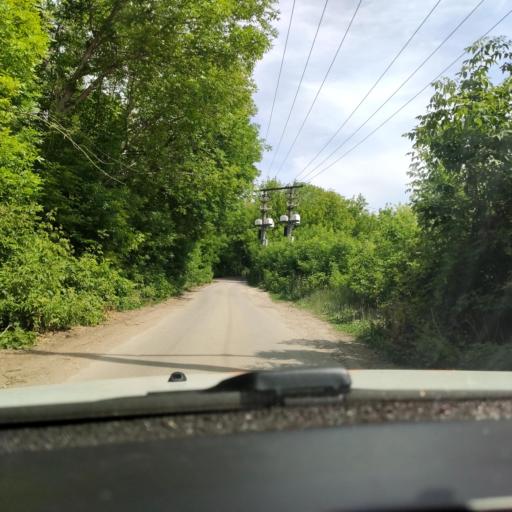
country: RU
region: Samara
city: Volzhskiy
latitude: 53.3447
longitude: 50.2024
